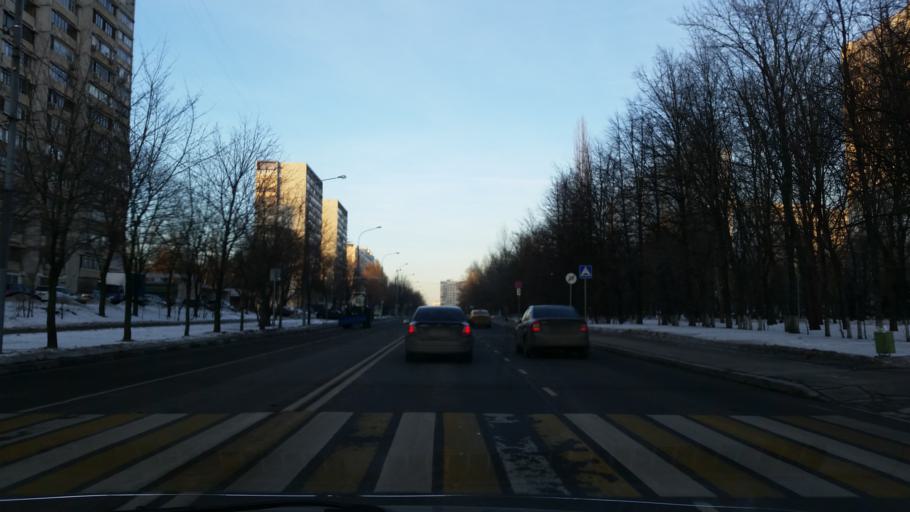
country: RU
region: Moscow
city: Nagornyy
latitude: 55.6266
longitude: 37.6108
